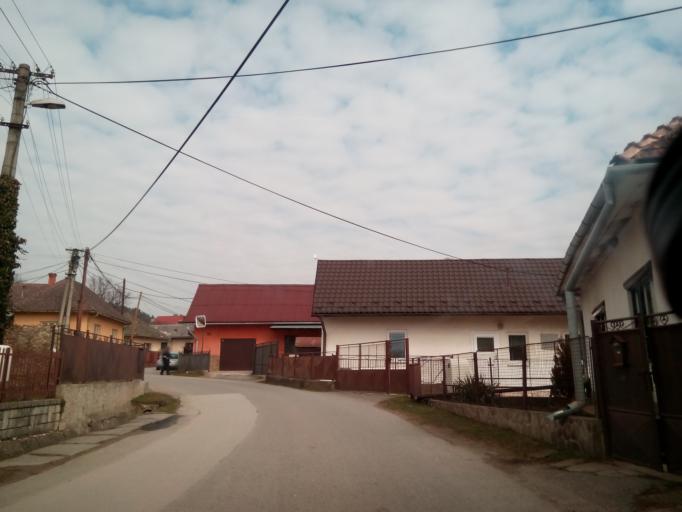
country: SK
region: Presovsky
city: Sabinov
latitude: 49.0482
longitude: 21.0163
